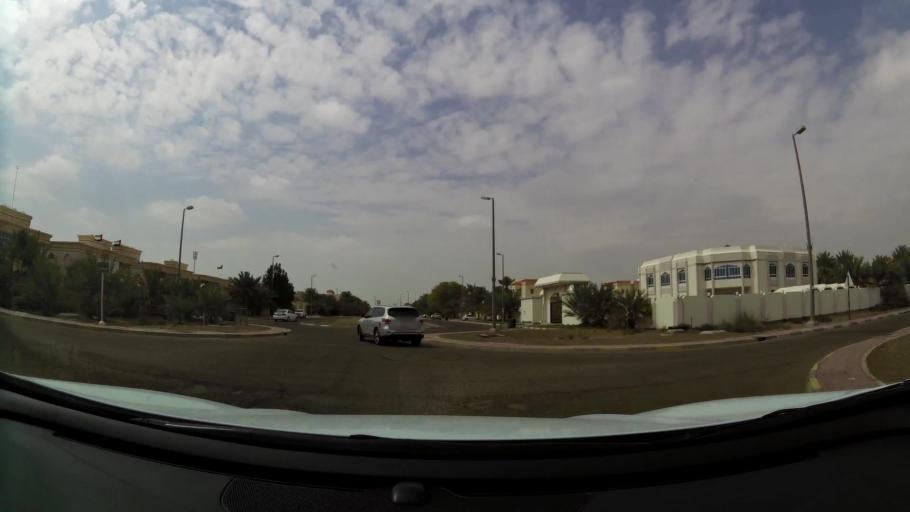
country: AE
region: Abu Dhabi
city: Al Ain
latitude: 24.2022
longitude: 55.8004
